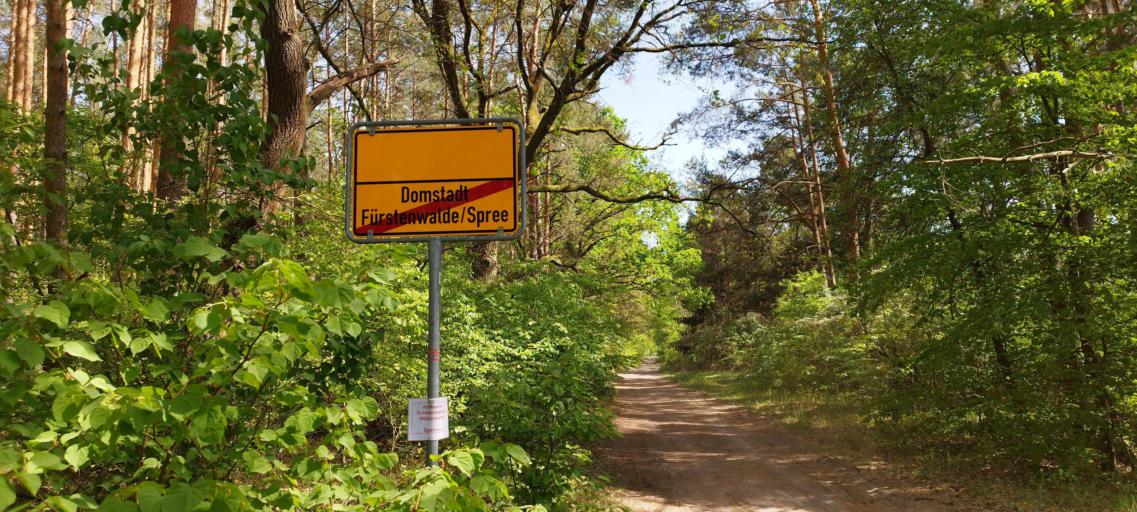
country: DE
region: Brandenburg
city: Furstenwalde
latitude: 52.3696
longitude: 14.0338
